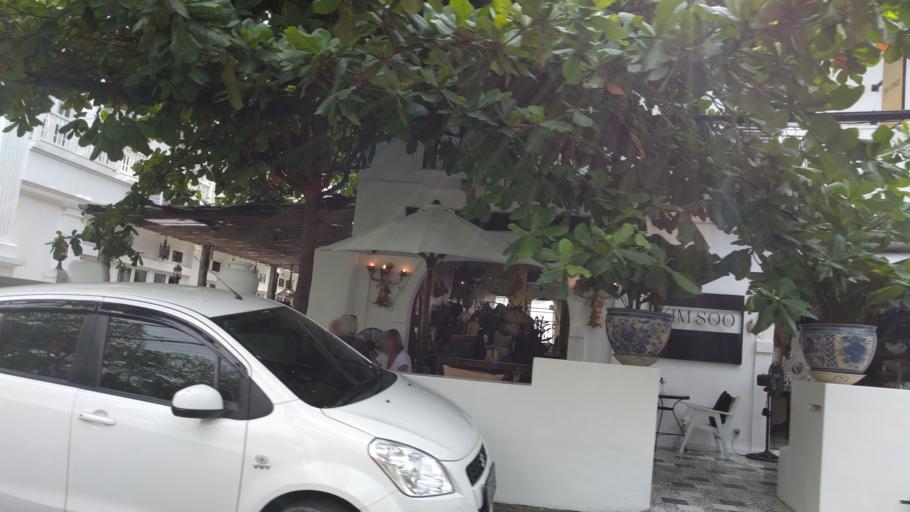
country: ID
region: Bali
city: Kuta
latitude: -8.6831
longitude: 115.1533
